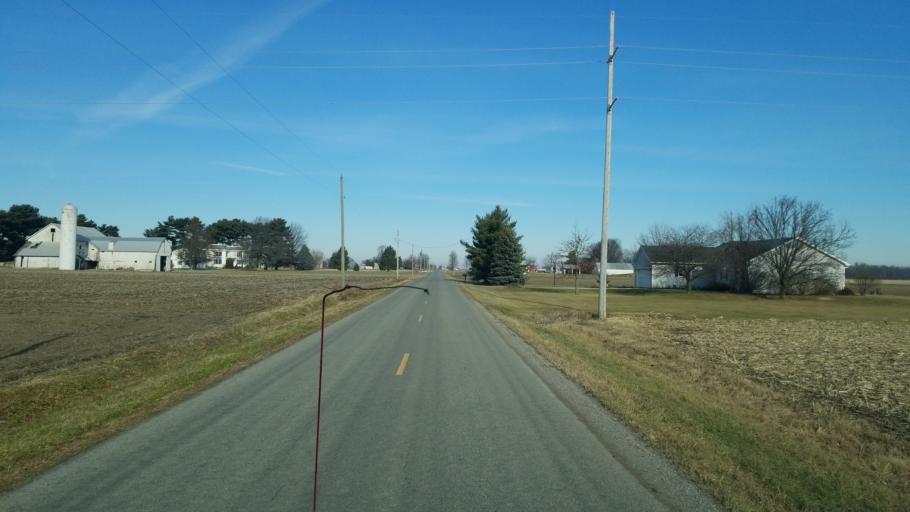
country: US
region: Ohio
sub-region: Putnam County
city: Pandora
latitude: 40.9406
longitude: -83.9379
